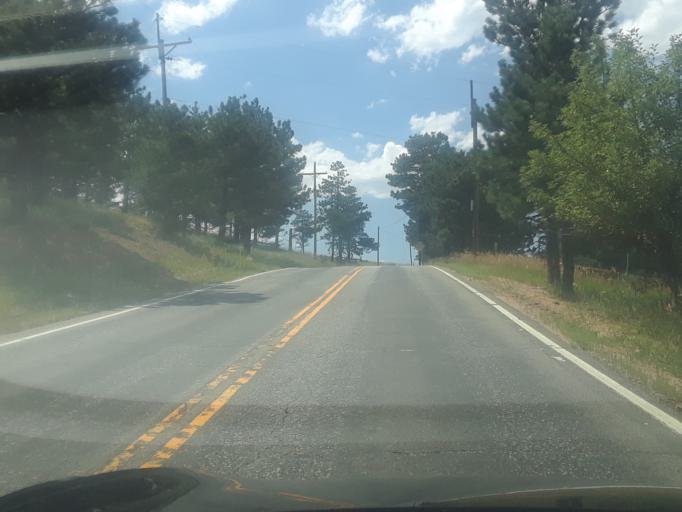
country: US
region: Colorado
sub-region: Boulder County
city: Boulder
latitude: 40.0481
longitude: -105.3425
